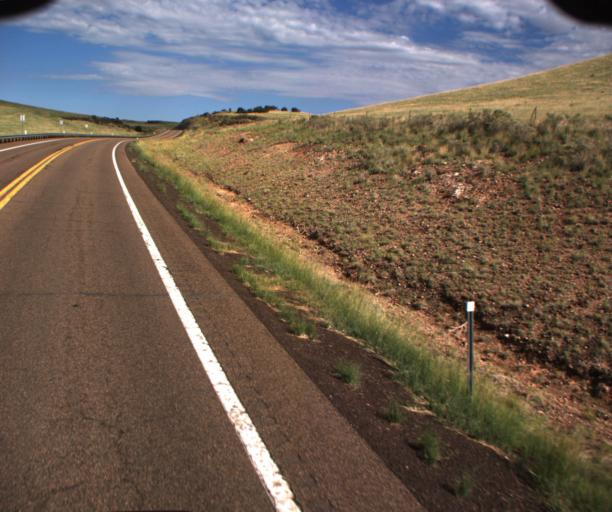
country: US
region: Arizona
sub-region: Apache County
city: Springerville
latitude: 34.2080
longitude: -109.4235
